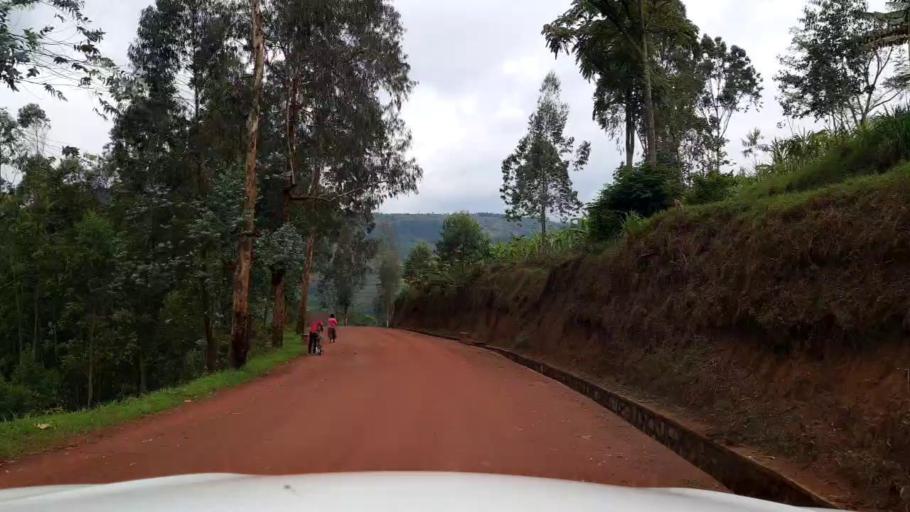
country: RW
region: Northern Province
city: Musanze
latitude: -1.6628
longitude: 29.8017
